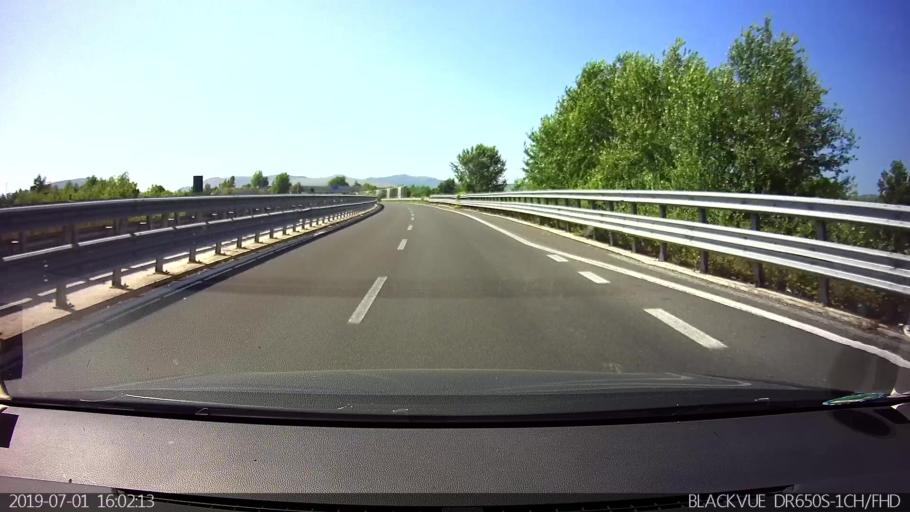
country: IT
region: Latium
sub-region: Provincia di Frosinone
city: Castelmassimo
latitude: 41.6678
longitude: 13.3606
